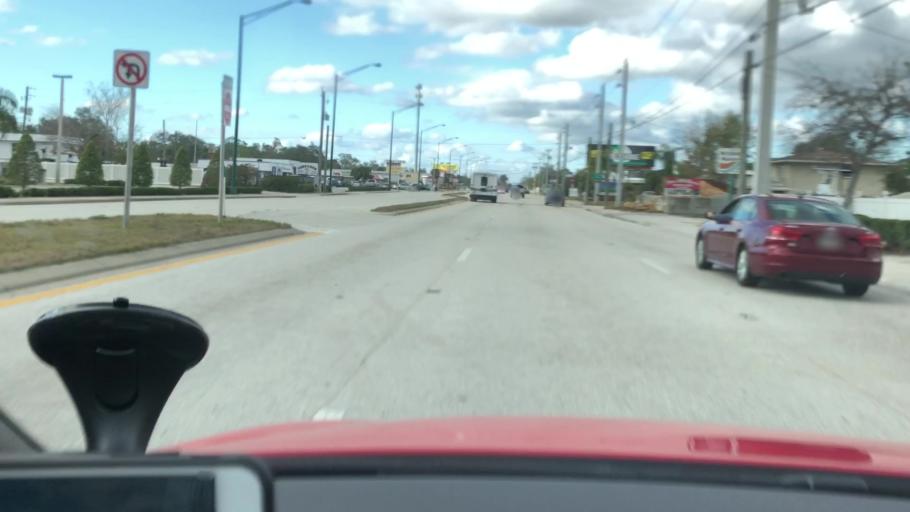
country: US
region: Florida
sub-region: Volusia County
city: Ormond Beach
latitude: 29.2544
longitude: -81.0719
